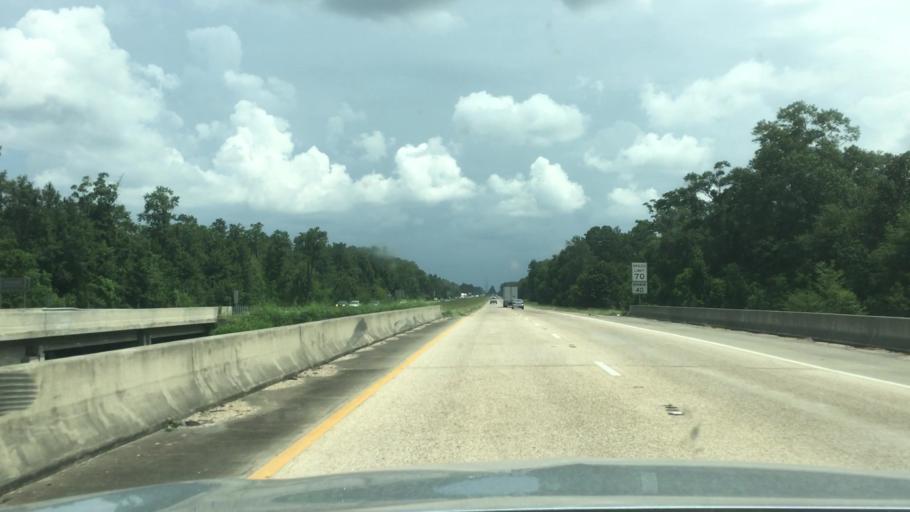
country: US
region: Mississippi
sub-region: Pearl River County
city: Picayune
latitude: 30.5283
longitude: -89.6578
